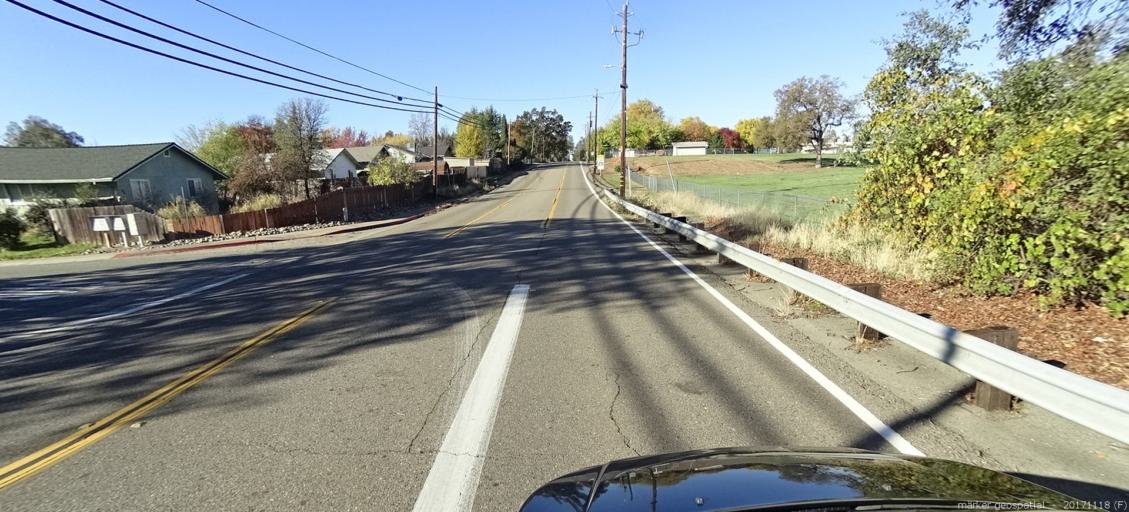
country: US
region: California
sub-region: Shasta County
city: Cottonwood
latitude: 40.3857
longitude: -122.2886
